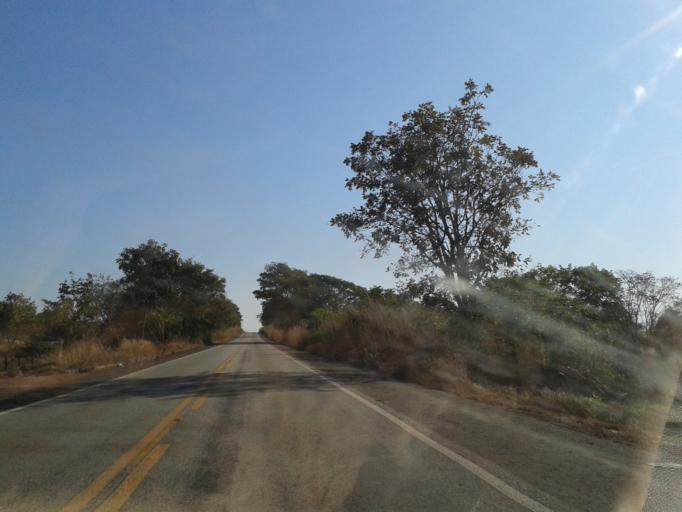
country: BR
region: Goias
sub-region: Mozarlandia
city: Mozarlandia
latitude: -14.9750
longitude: -50.5806
